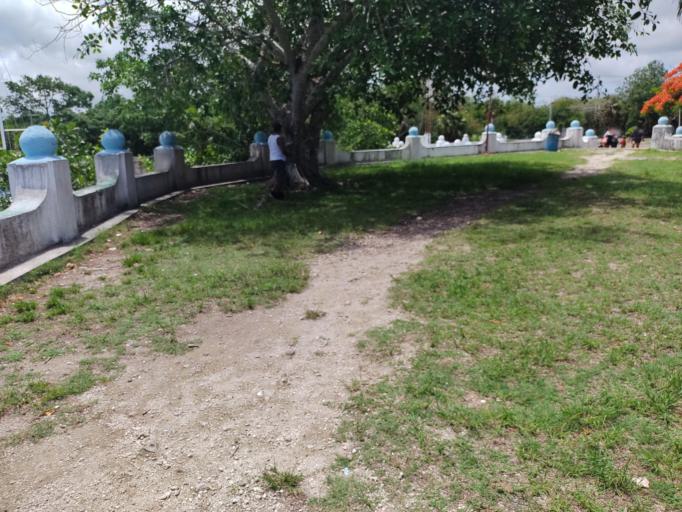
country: MX
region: Quintana Roo
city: San Miguel de Cozumel
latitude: 20.5272
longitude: -86.9407
